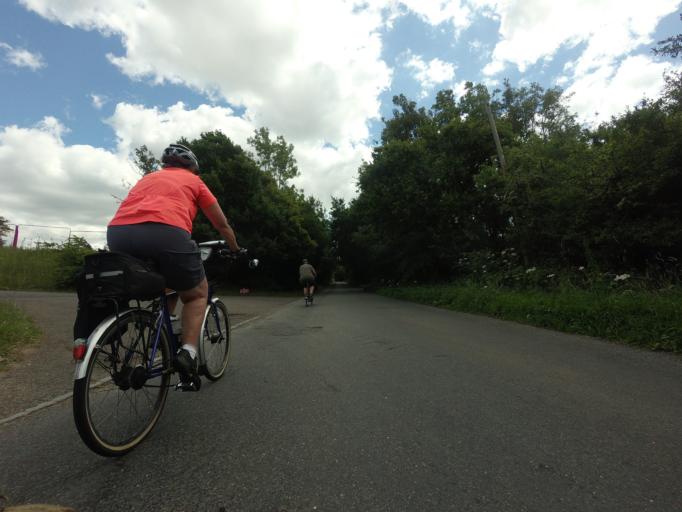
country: GB
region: England
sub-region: East Sussex
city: Hailsham
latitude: 50.8406
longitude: 0.1827
